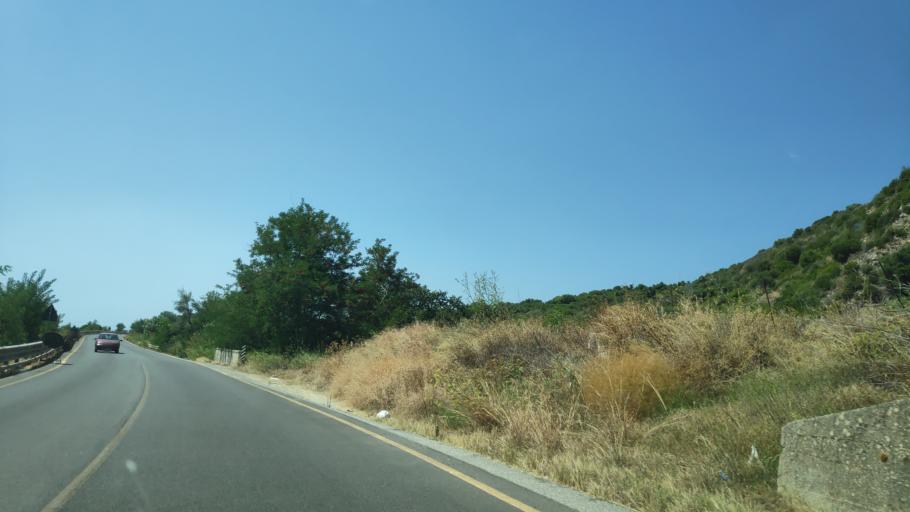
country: IT
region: Calabria
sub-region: Provincia di Reggio Calabria
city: Africo Nuovo
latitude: 38.0261
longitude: 16.1396
